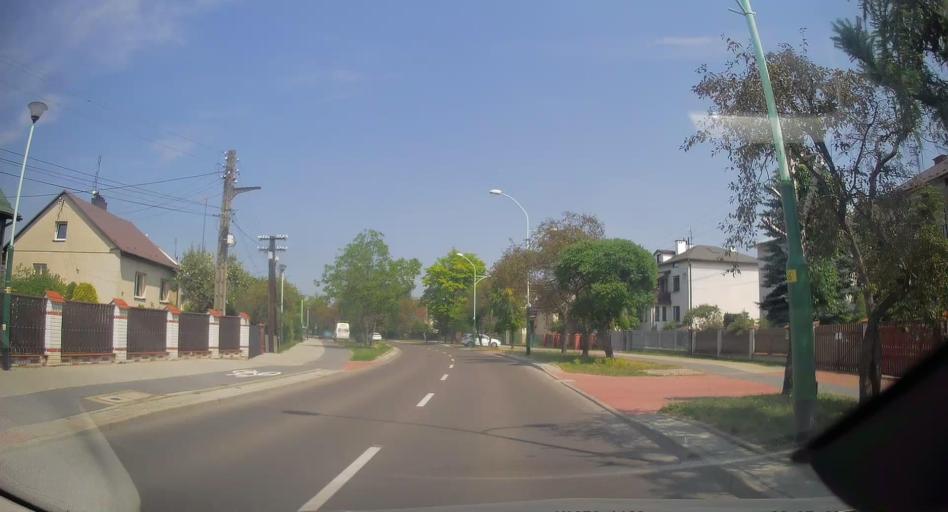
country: PL
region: Subcarpathian Voivodeship
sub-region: Powiat debicki
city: Debica
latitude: 50.0518
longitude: 21.4295
